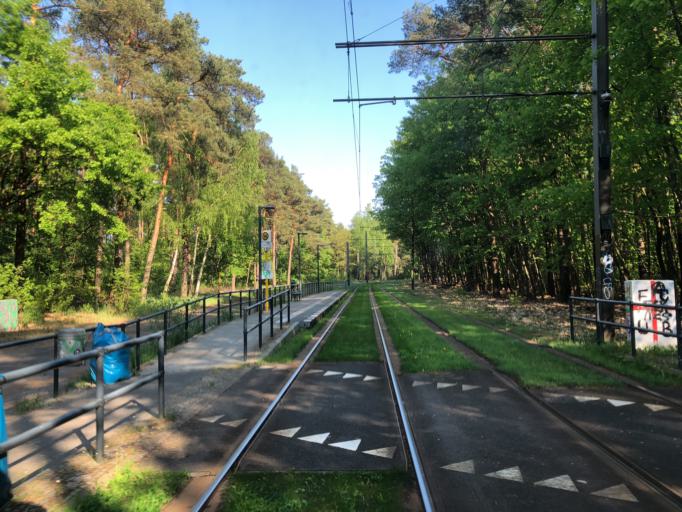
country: DE
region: Brandenburg
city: Zeuthen
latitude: 52.4059
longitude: 13.6209
